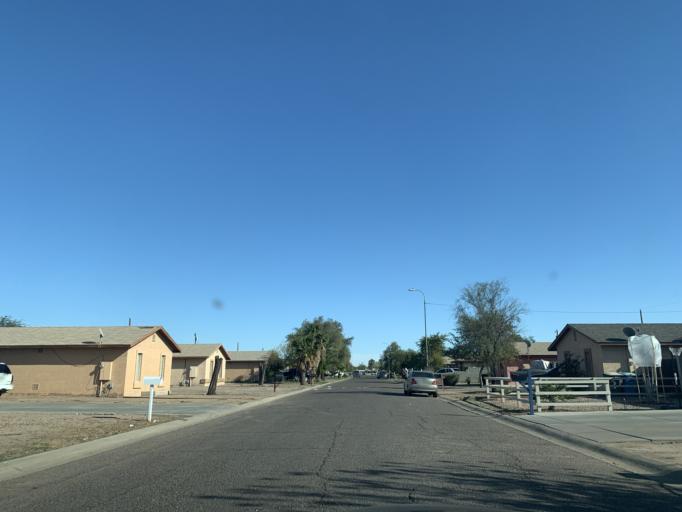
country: US
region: Arizona
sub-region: Maricopa County
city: Laveen
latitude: 33.3966
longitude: -112.1409
